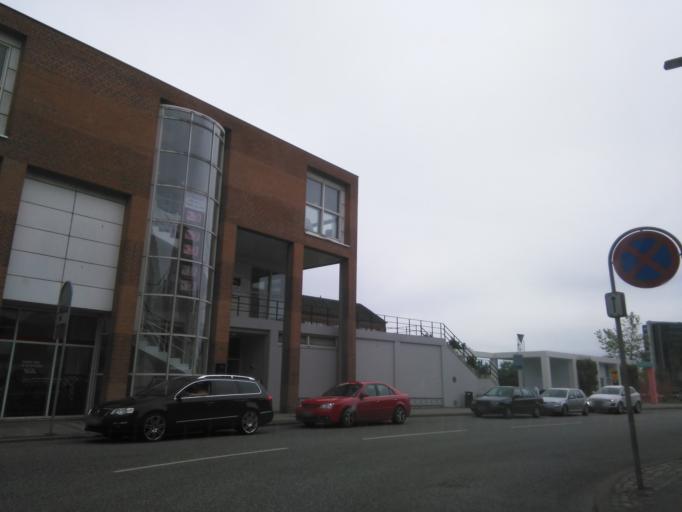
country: DK
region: Central Jutland
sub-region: Horsens Kommune
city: Horsens
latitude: 55.8605
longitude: 9.8469
